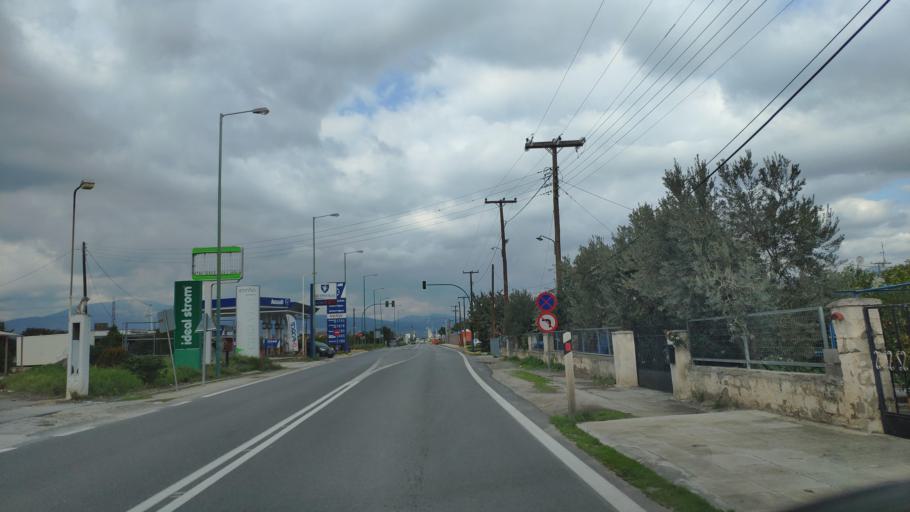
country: GR
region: Peloponnese
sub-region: Nomos Argolidos
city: Argos
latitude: 37.6515
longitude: 22.7285
